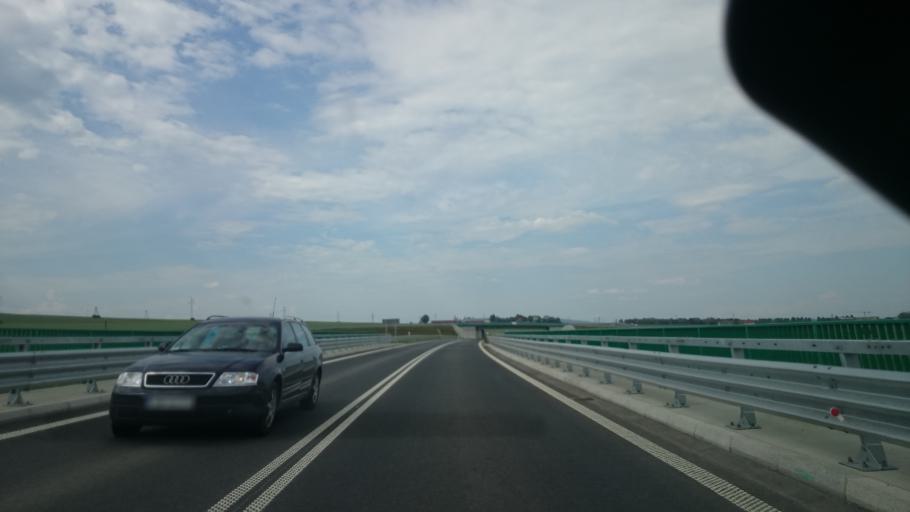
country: PL
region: Lower Silesian Voivodeship
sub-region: Powiat klodzki
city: Klodzko
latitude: 50.4169
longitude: 16.6254
